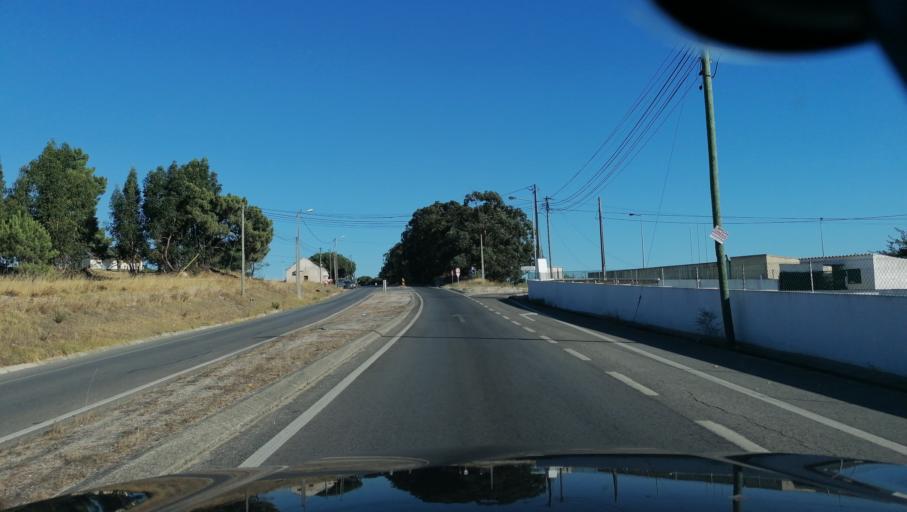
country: PT
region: Setubal
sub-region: Moita
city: Moita
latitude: 38.6328
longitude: -8.9695
